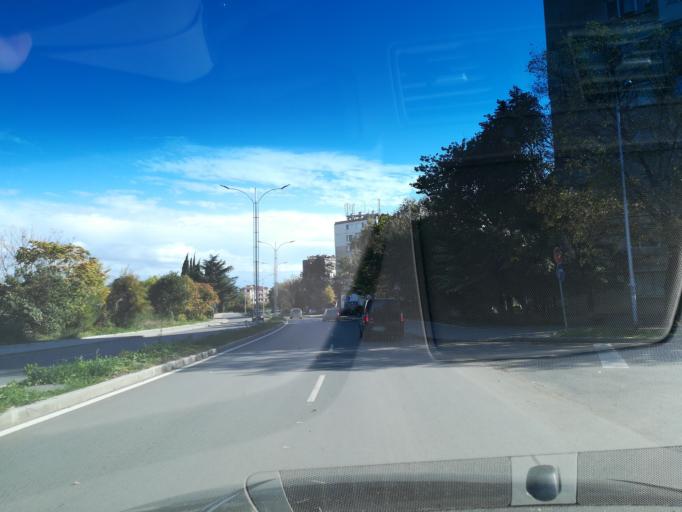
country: BG
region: Stara Zagora
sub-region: Obshtina Stara Zagora
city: Stara Zagora
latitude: 42.4301
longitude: 25.6447
